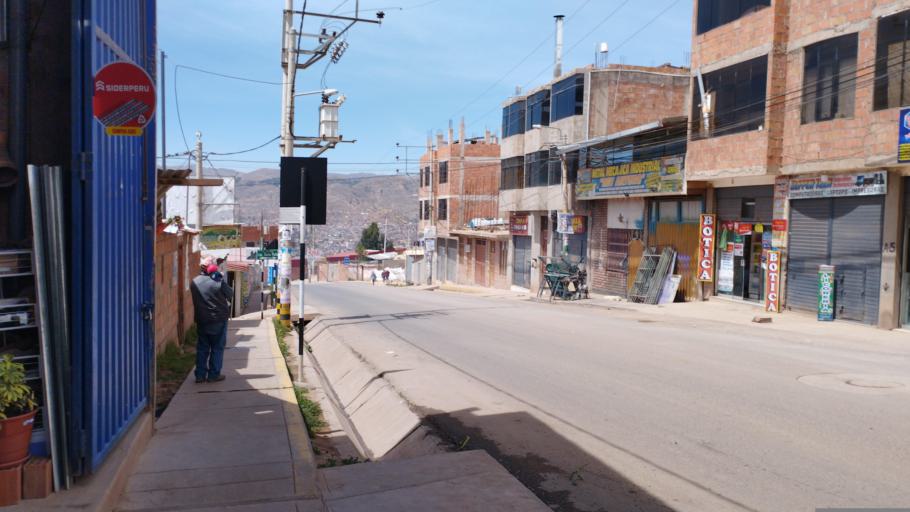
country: PE
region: Cusco
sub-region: Provincia de Cusco
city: Cusco
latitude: -13.5225
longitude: -71.9271
